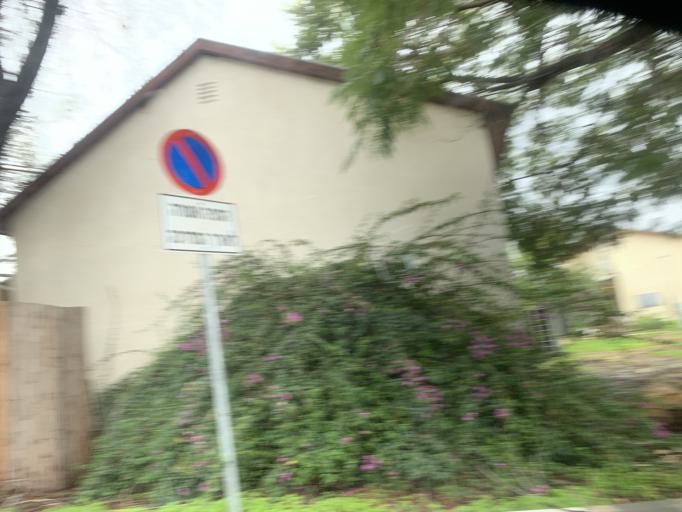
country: PS
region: West Bank
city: Qalqilyah
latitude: 32.2131
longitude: 34.9784
